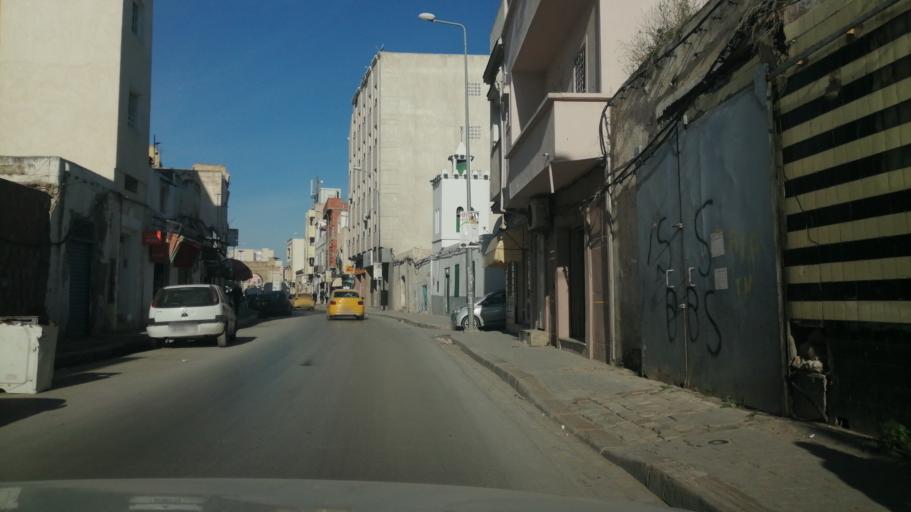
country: TN
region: Tunis
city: Tunis
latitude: 36.8076
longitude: 10.1615
